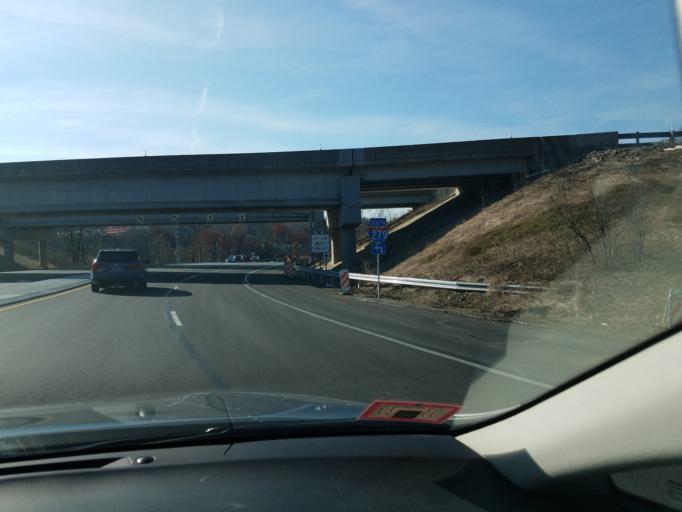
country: US
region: Pennsylvania
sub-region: Allegheny County
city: Ben Avon
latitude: 40.5254
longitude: -80.0700
